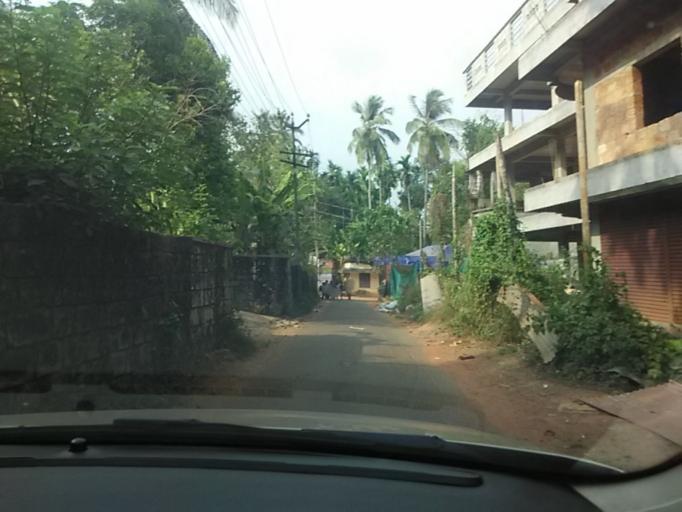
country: IN
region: Kerala
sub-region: Kozhikode
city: Naduvannur
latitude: 11.5581
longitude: 75.7581
